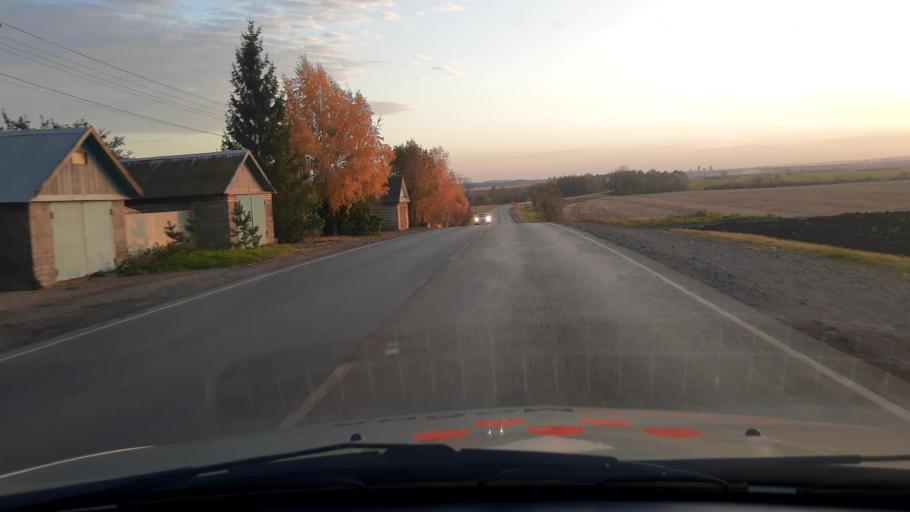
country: RU
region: Bashkortostan
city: Ufa
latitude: 54.8210
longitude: 55.9862
